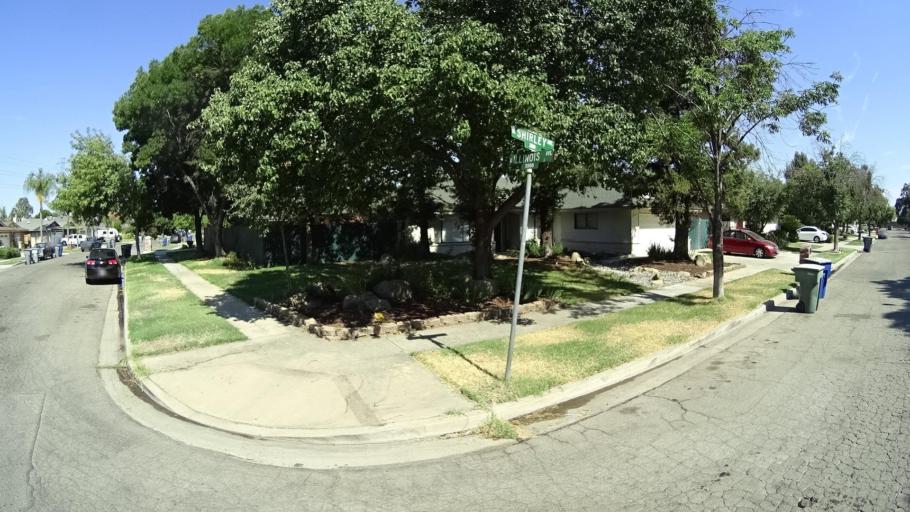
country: US
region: California
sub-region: Fresno County
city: Sunnyside
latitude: 36.7451
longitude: -119.6834
